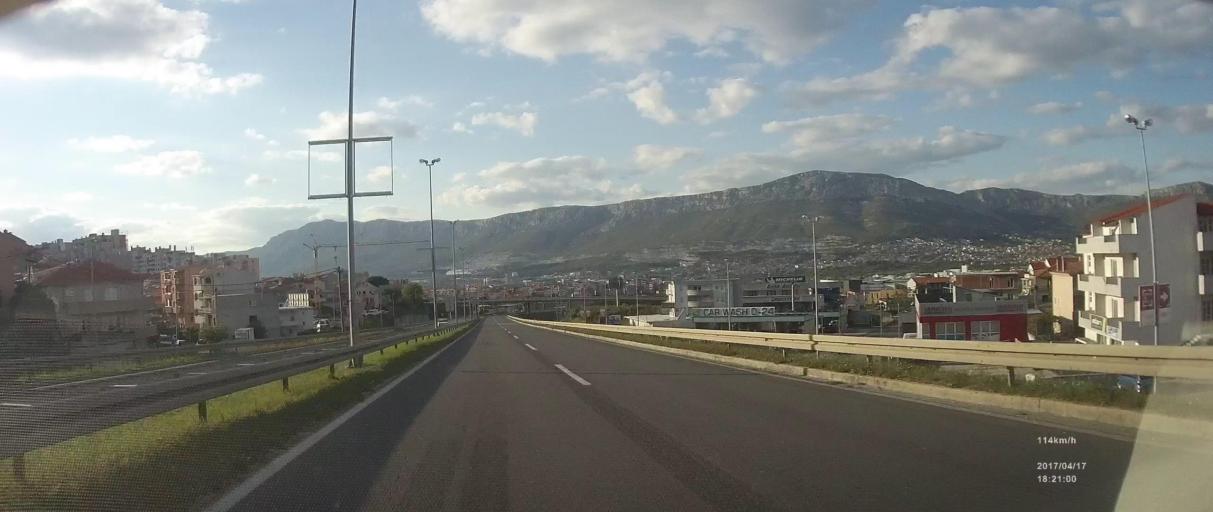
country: HR
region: Splitsko-Dalmatinska
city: Vranjic
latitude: 43.5136
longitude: 16.4831
